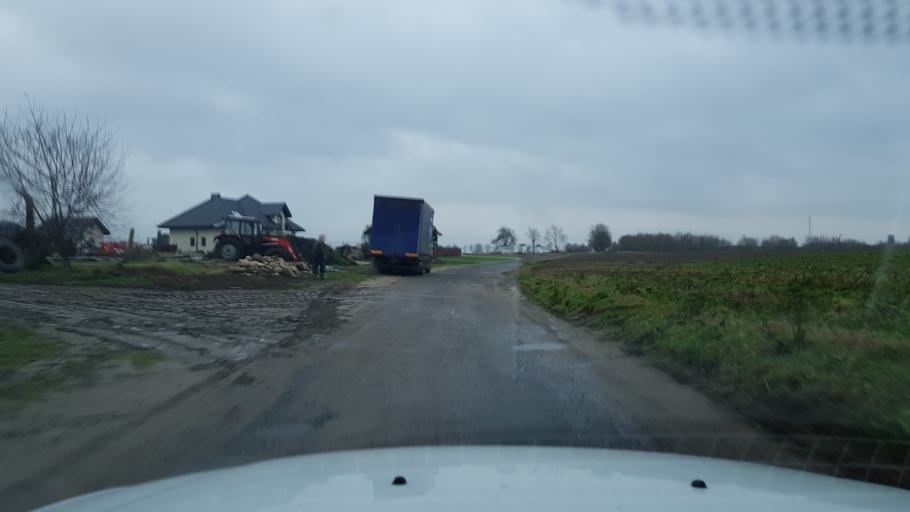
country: PL
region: West Pomeranian Voivodeship
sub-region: Powiat gryficki
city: Brojce
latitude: 53.9636
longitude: 15.3001
